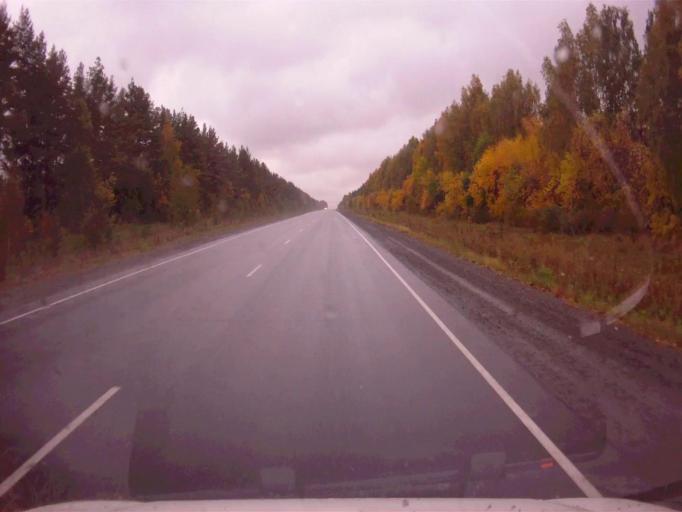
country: RU
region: Chelyabinsk
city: Roshchino
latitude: 55.3757
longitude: 61.1504
